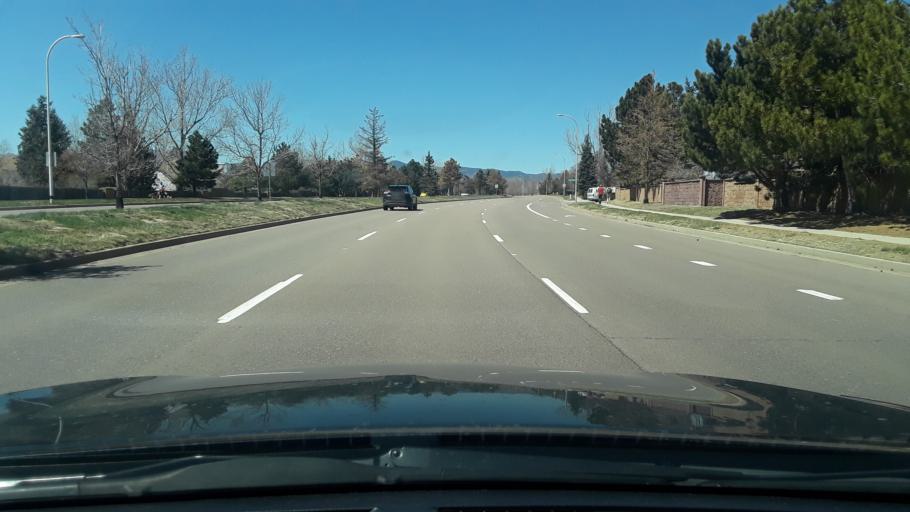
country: US
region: Colorado
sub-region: El Paso County
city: Black Forest
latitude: 38.9549
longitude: -104.7448
